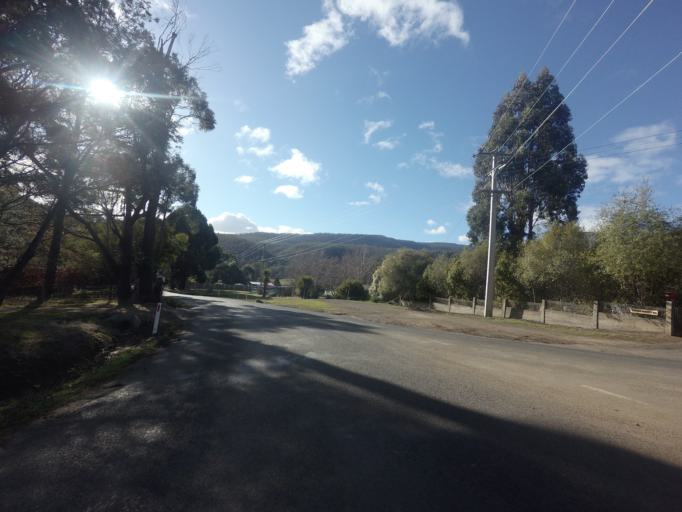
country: AU
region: Tasmania
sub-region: Derwent Valley
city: New Norfolk
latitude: -42.8053
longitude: 147.1373
